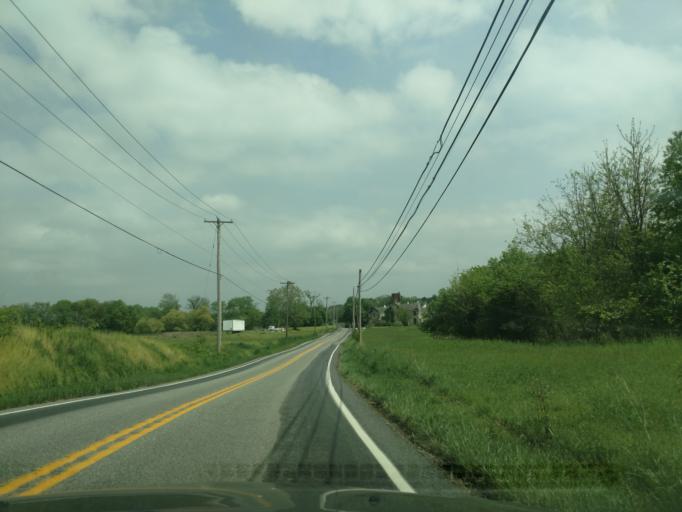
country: US
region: Pennsylvania
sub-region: Chester County
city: Spring City
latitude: 40.1541
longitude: -75.5645
